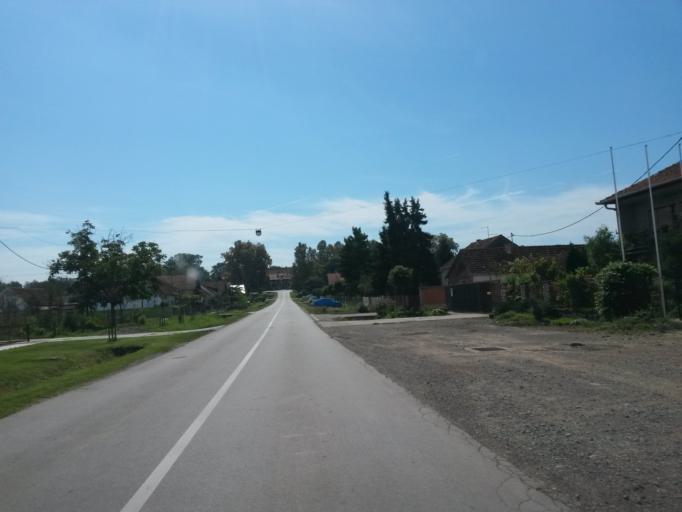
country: HR
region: Vukovarsko-Srijemska
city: Nustar
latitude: 45.3323
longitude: 18.8352
